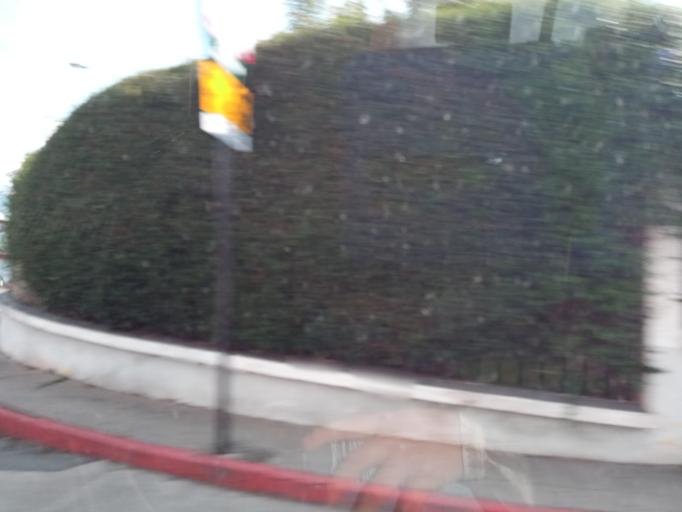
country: GT
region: Quetzaltenango
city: Quetzaltenango
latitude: 14.8546
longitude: -91.5381
